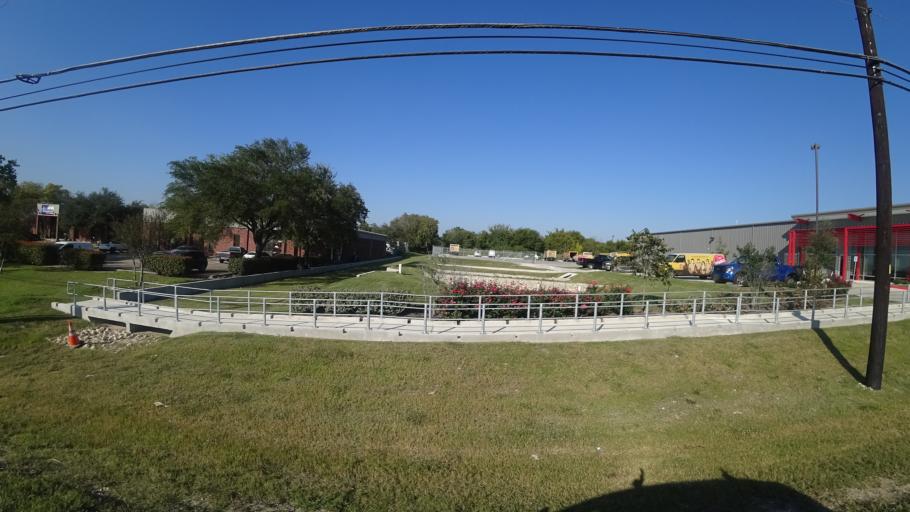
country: US
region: Texas
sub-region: Travis County
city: Wells Branch
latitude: 30.3454
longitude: -97.6752
